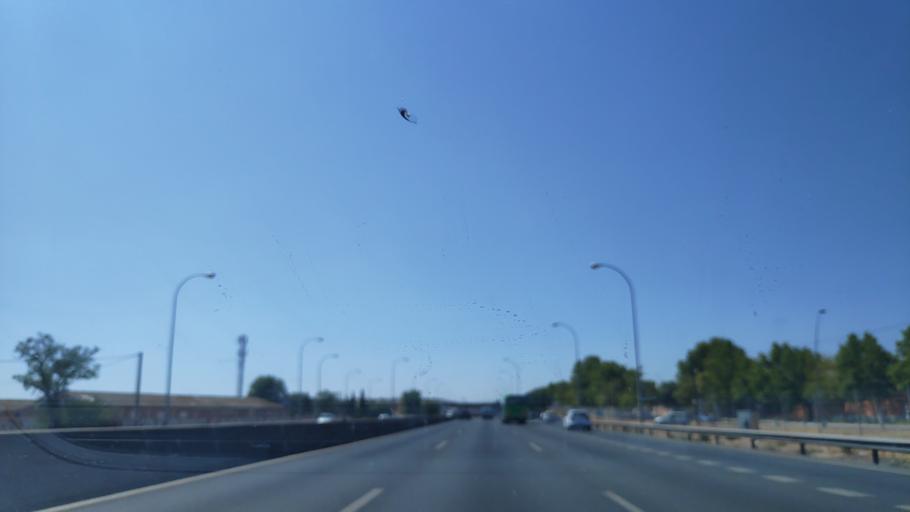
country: ES
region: Madrid
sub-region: Provincia de Madrid
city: Getafe
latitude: 40.2839
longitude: -3.7454
